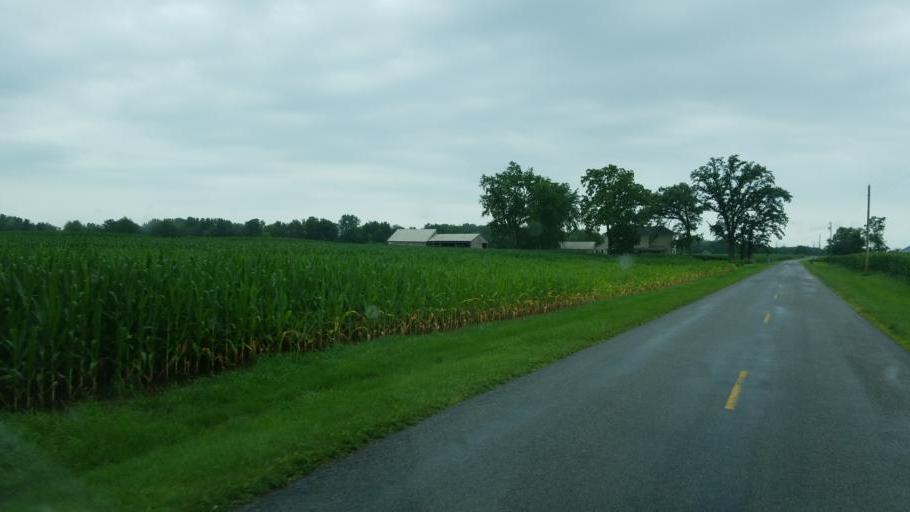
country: US
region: Ohio
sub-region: Hardin County
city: Kenton
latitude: 40.5108
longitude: -83.4743
